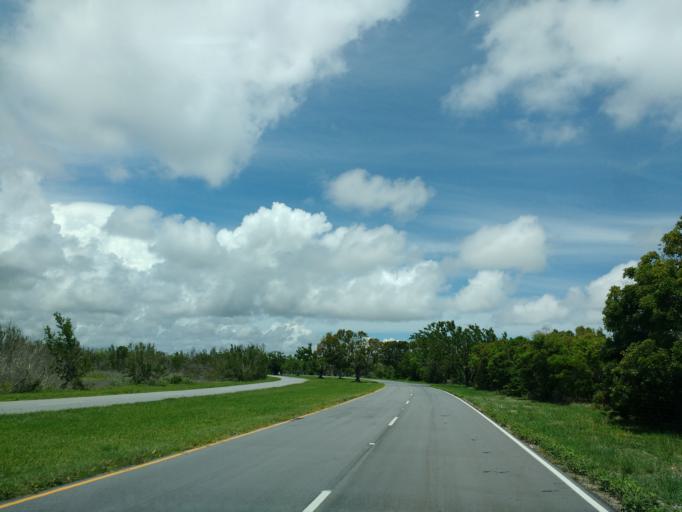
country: US
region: Florida
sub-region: Monroe County
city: Islamorada
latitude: 25.1400
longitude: -80.9284
